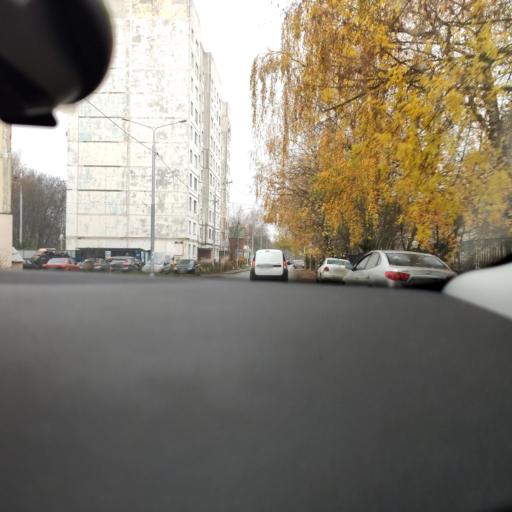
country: RU
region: Moskovskaya
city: Dedovsk
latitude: 55.8567
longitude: 37.1279
